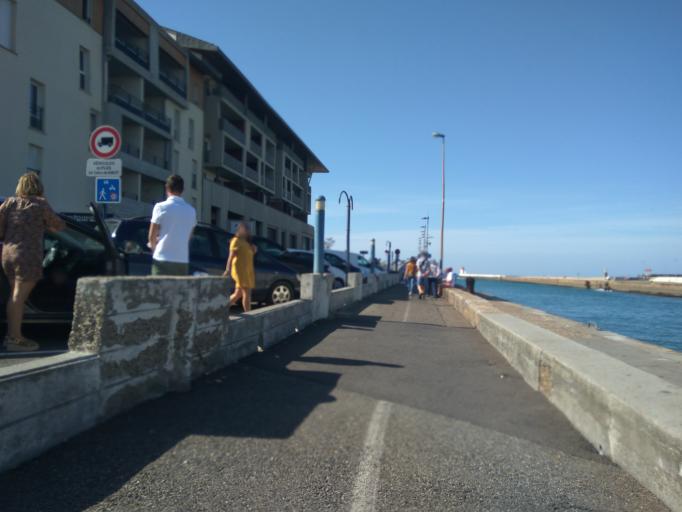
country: FR
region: Aquitaine
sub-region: Departement des Landes
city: Capbreton
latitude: 43.6546
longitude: -1.4431
